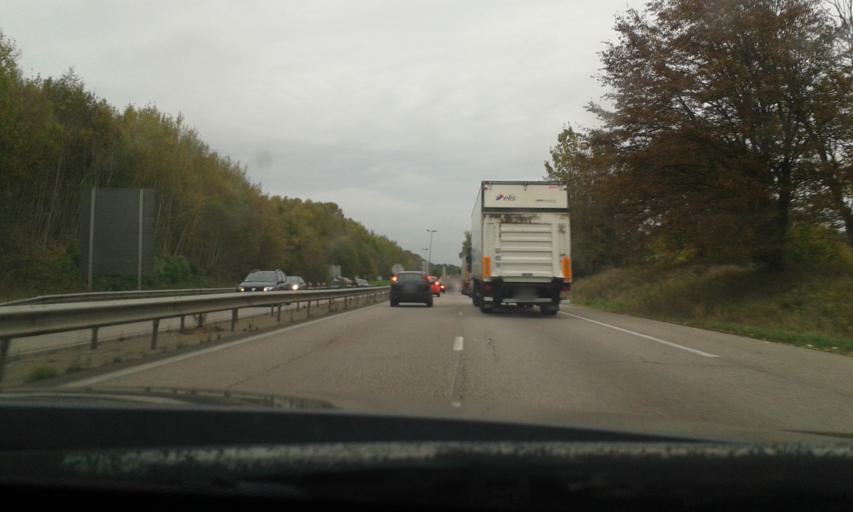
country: FR
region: Haute-Normandie
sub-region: Departement de la Seine-Maritime
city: Oissel
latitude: 49.3443
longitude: 1.0765
